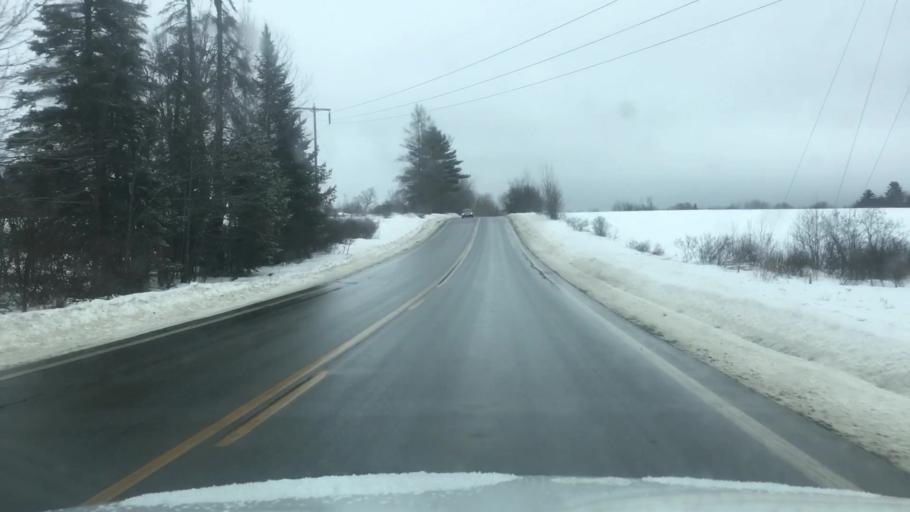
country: US
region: Maine
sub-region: Franklin County
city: Chesterville
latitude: 44.5894
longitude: -70.1482
